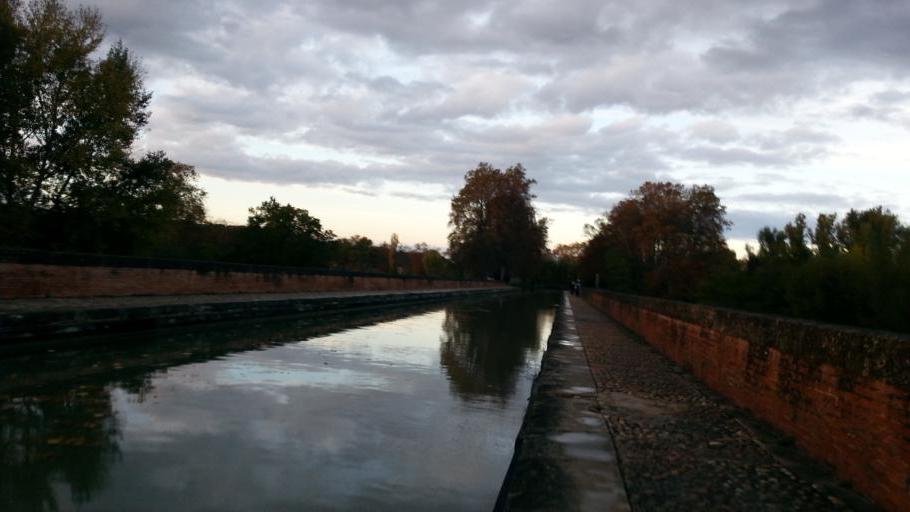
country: FR
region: Midi-Pyrenees
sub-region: Departement du Tarn-et-Garonne
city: Moissac
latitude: 44.0920
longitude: 1.1026
